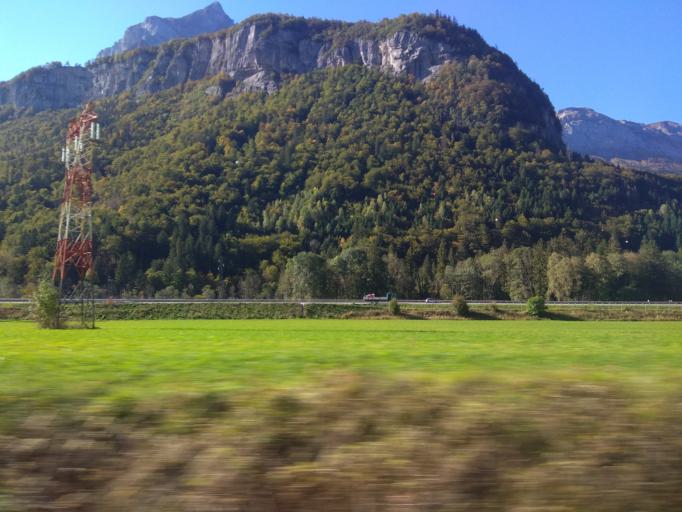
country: FR
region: Rhone-Alpes
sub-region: Departement de la Haute-Savoie
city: Magland
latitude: 45.9853
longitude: 6.6314
